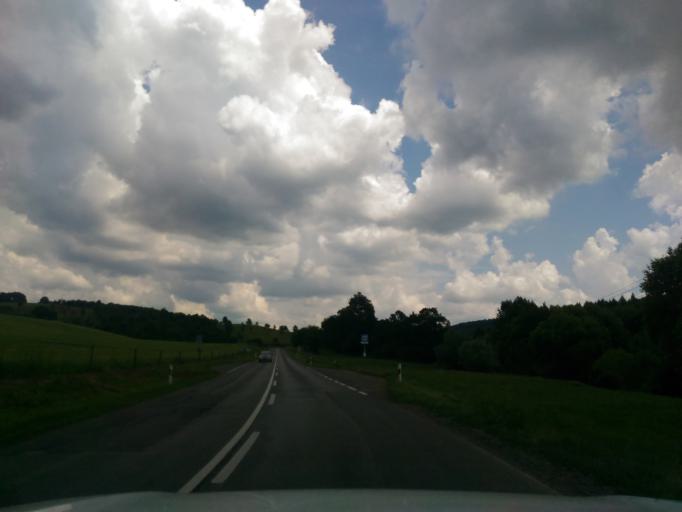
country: HU
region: Baranya
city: Komlo
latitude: 46.1610
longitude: 18.2158
